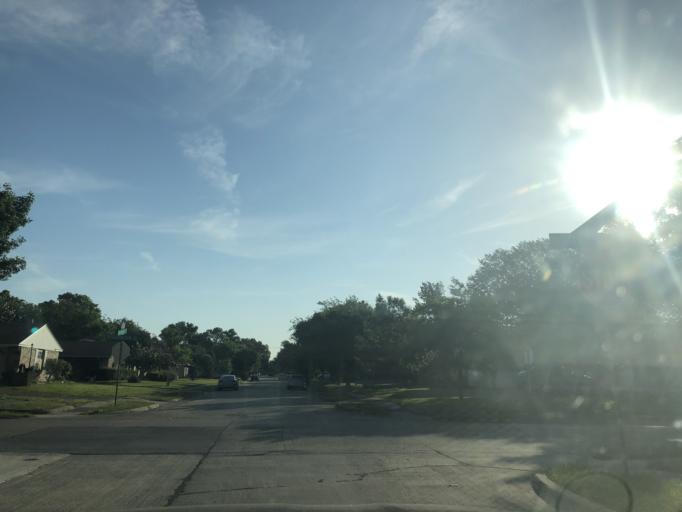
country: US
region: Texas
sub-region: Dallas County
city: Garland
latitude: 32.8482
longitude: -96.6346
